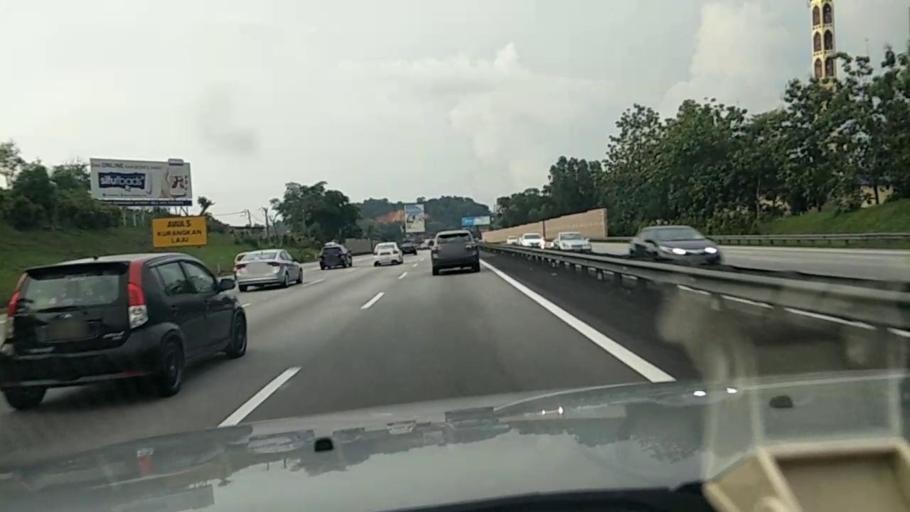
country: MY
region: Selangor
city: Kuang
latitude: 3.2433
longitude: 101.5656
